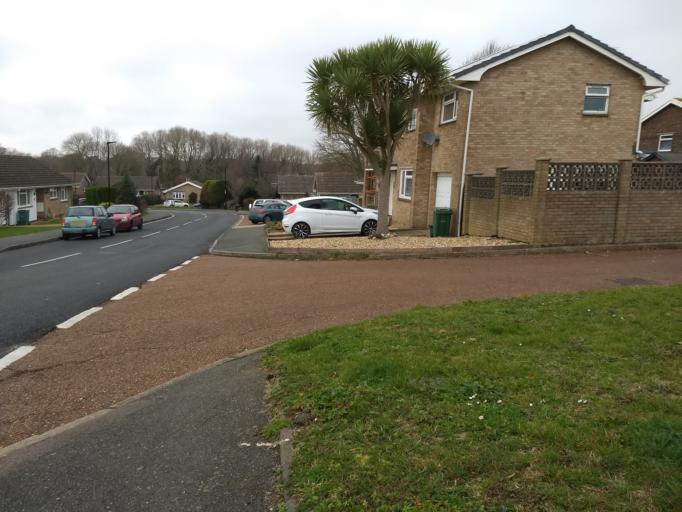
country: GB
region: England
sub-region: Isle of Wight
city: Sandown
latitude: 50.6621
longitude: -1.1602
